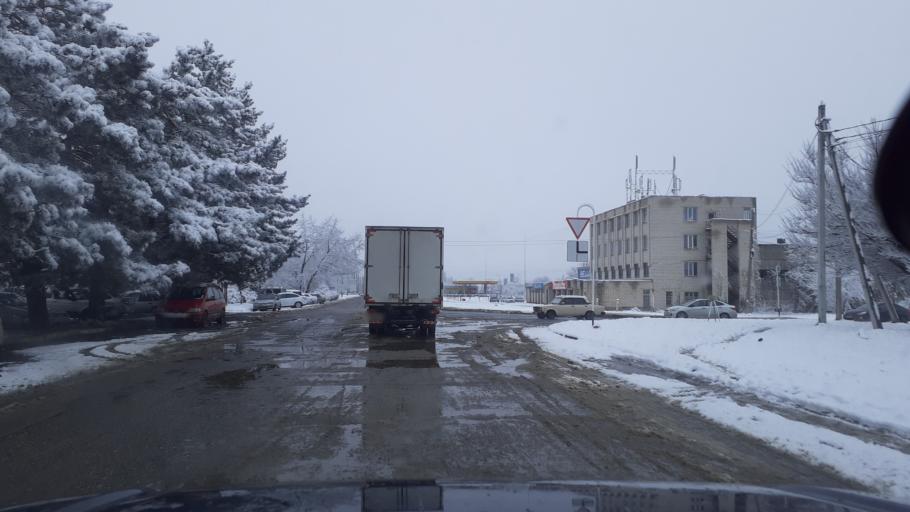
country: RU
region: Adygeya
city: Maykop
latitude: 44.6342
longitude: 40.1249
